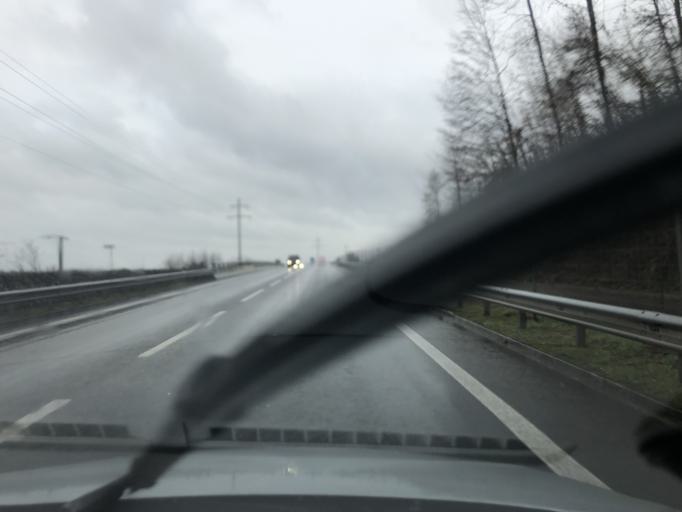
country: CH
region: Aargau
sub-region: Bezirk Brugg
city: Hausen
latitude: 47.4537
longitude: 8.2122
